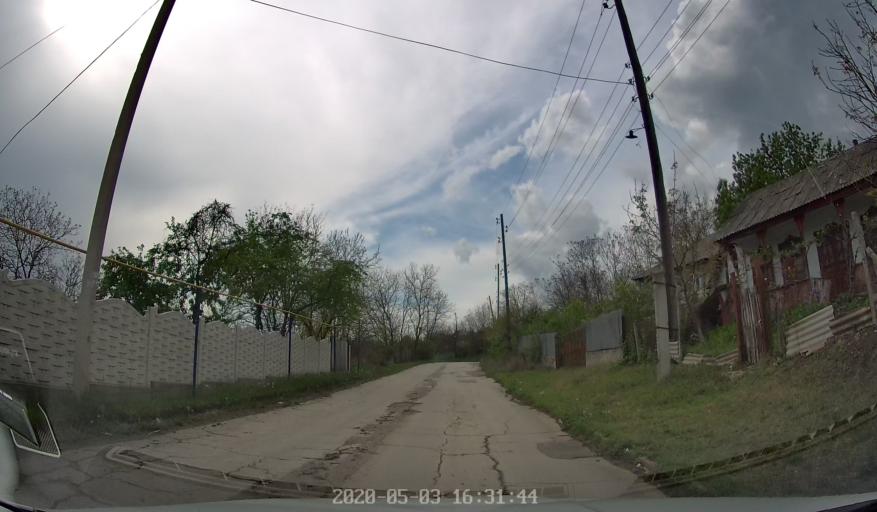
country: MD
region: Calarasi
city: Calarasi
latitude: 47.1915
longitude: 28.3381
